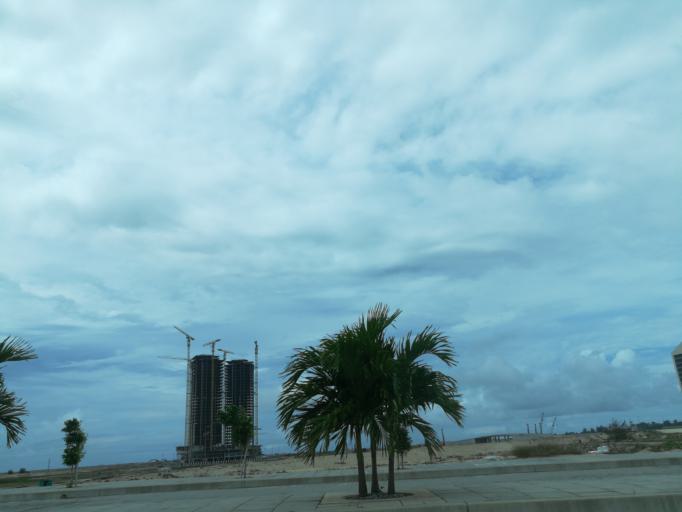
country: NG
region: Lagos
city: Lagos
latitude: 6.4097
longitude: 3.4080
